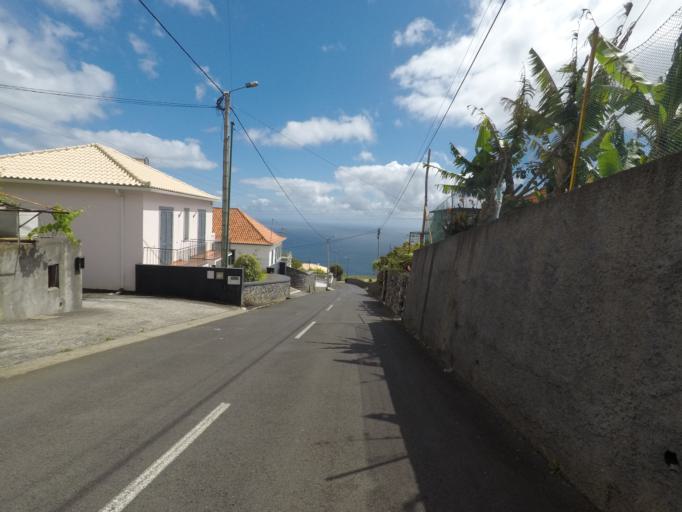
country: PT
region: Madeira
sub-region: Calheta
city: Estreito da Calheta
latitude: 32.7336
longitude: -17.1838
